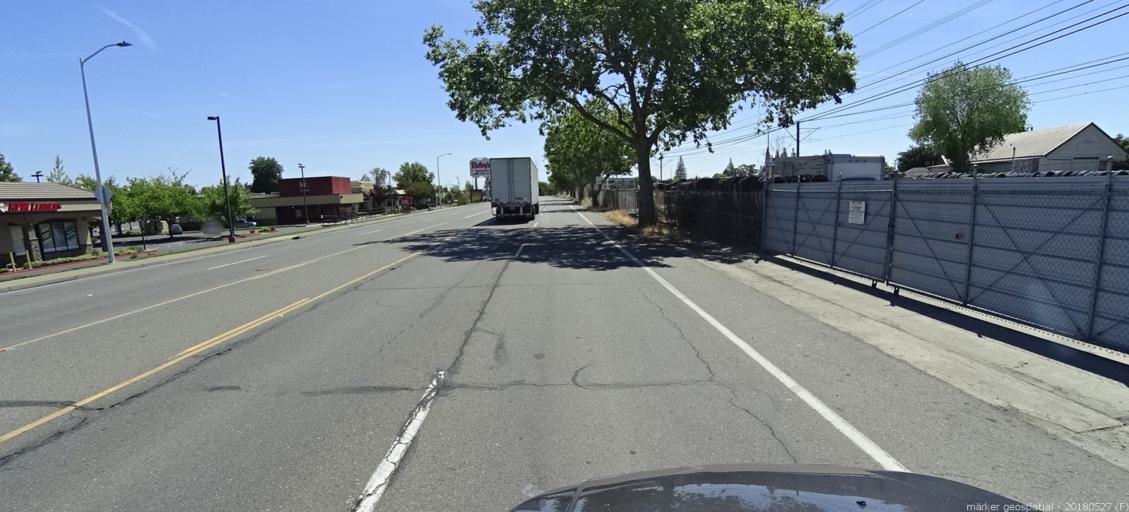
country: US
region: California
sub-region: Sacramento County
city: Rosemont
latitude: 38.5470
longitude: -121.3978
